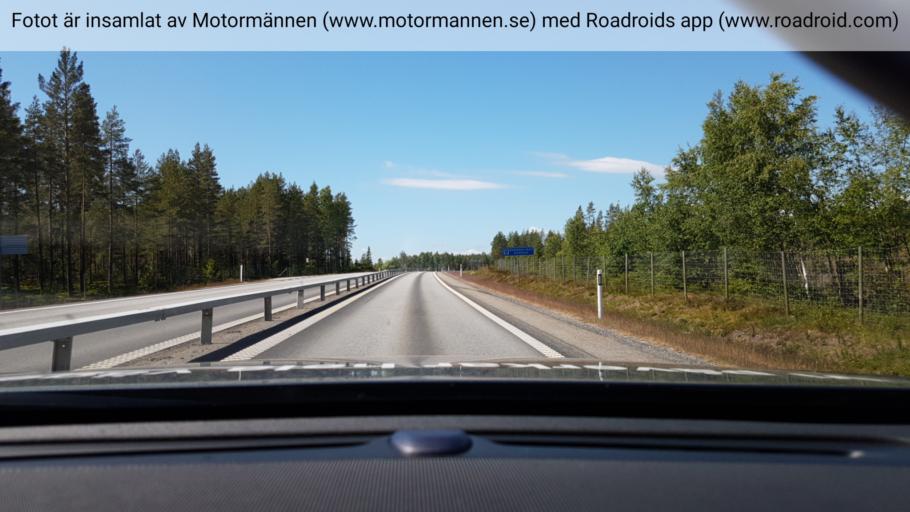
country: SE
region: Vaesterbotten
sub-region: Umea Kommun
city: Hoernefors
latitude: 63.6003
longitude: 19.7518
